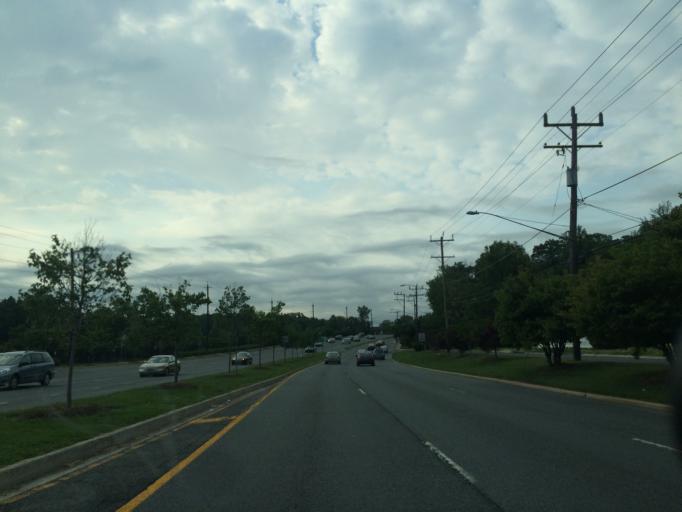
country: US
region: Maryland
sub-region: Montgomery County
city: White Oak
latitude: 39.0332
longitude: -76.9859
